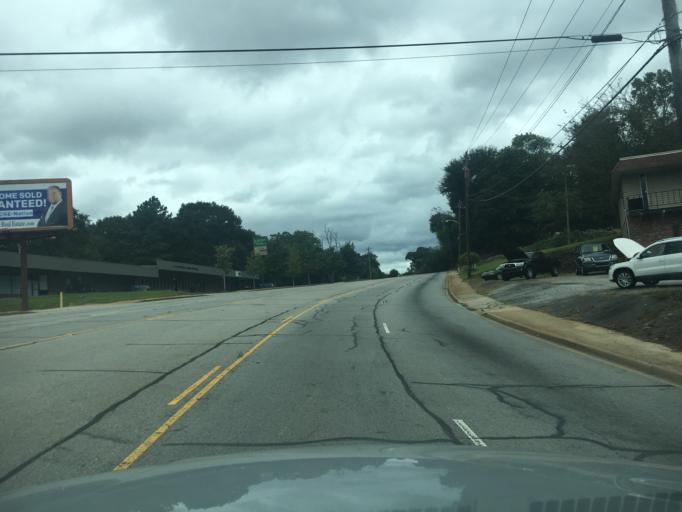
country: US
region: South Carolina
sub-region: Greenville County
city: Greenville
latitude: 34.8747
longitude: -82.3950
